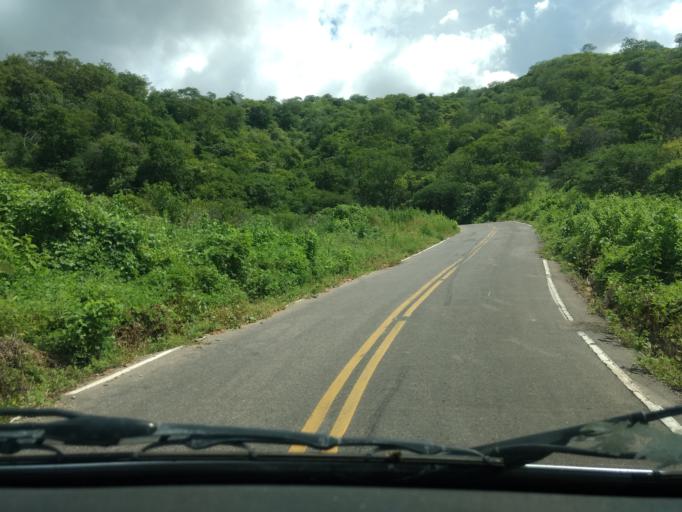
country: BR
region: Ceara
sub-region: Crateus
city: Crateus
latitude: -5.2405
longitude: -40.8977
